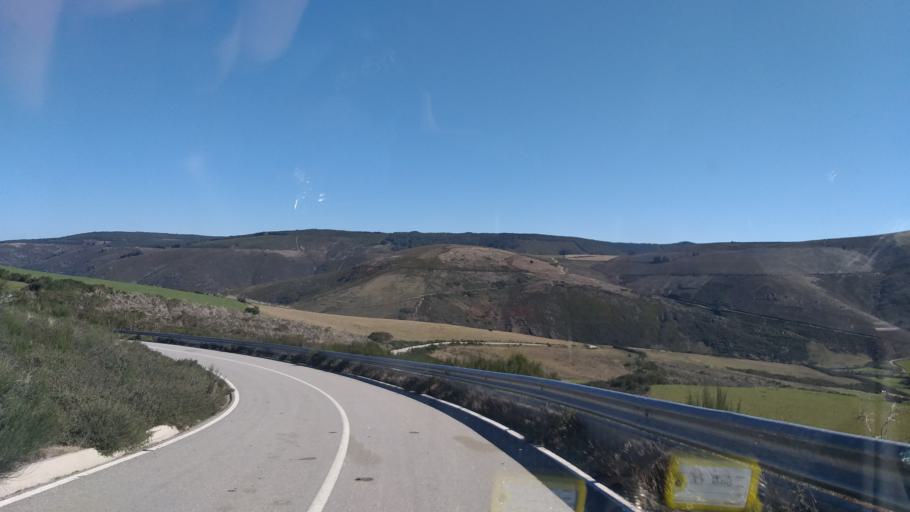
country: PT
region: Guarda
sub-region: Manteigas
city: Manteigas
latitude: 40.4630
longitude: -7.5022
